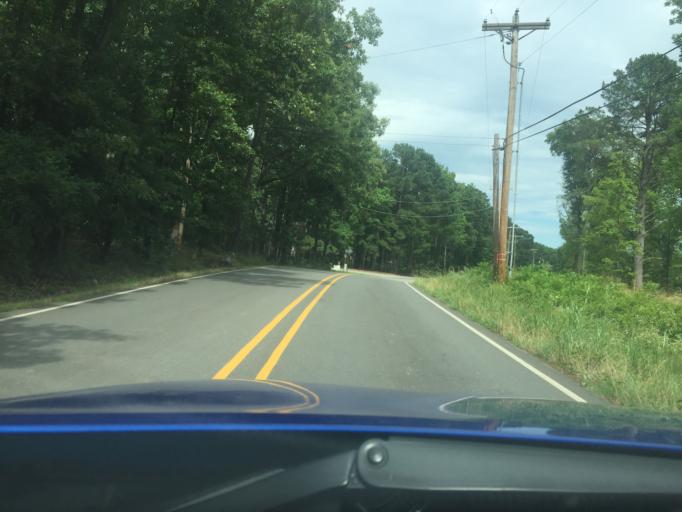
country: US
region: Arkansas
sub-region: Pulaski County
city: Maumelle
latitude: 34.8306
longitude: -92.4413
